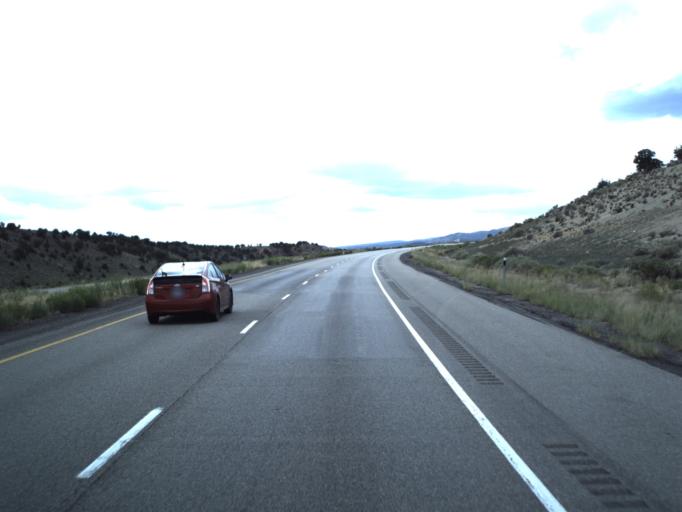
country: US
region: Utah
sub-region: Emery County
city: Ferron
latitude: 38.7851
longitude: -111.3031
